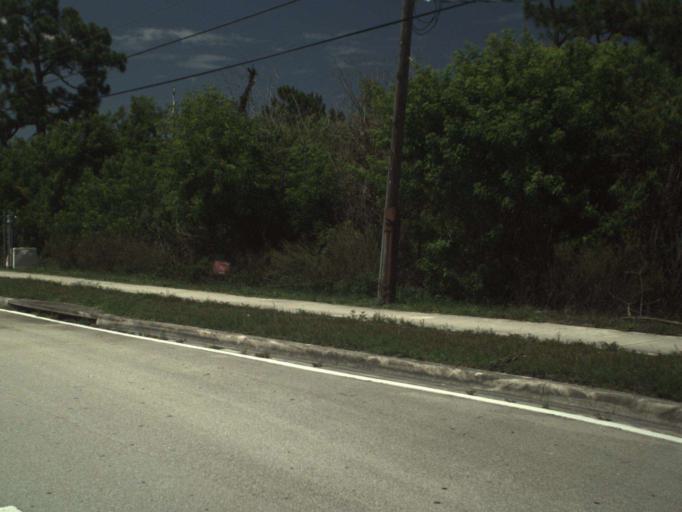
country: US
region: Florida
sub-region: Saint Lucie County
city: River Park
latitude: 27.3142
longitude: -80.3134
